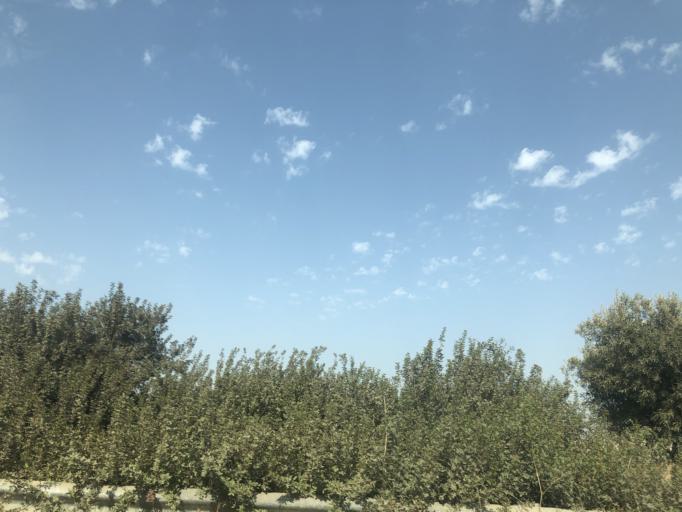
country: IL
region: Central District
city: Rosh Ha'Ayin
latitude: 32.0838
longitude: 34.9443
